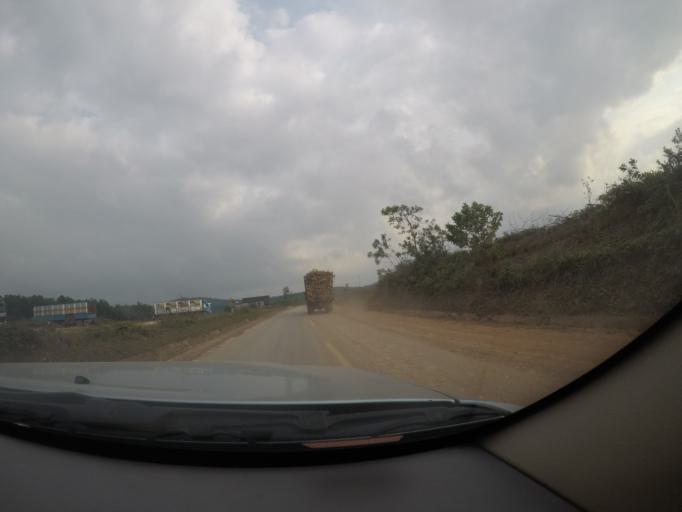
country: VN
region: Quang Tri
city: Ho Xa
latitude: 17.0837
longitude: 106.8613
